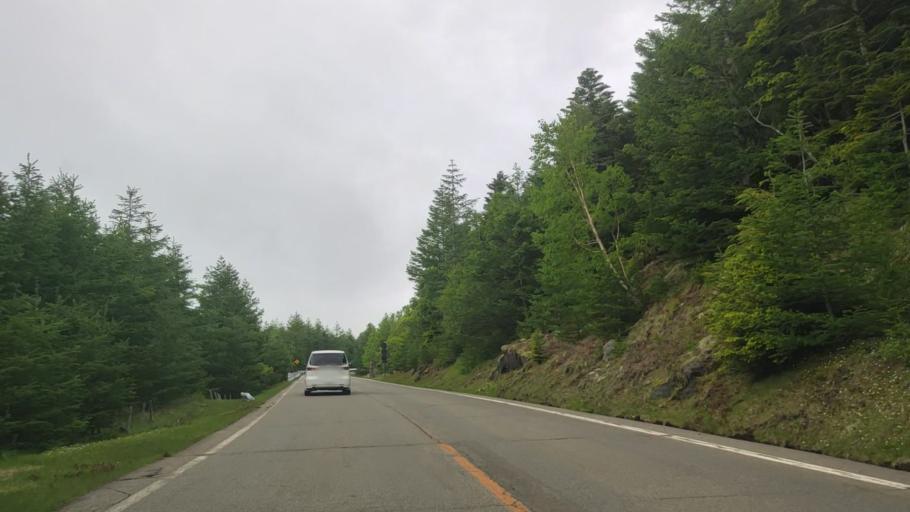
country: JP
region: Yamanashi
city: Fujikawaguchiko
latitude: 35.3869
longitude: 138.6975
